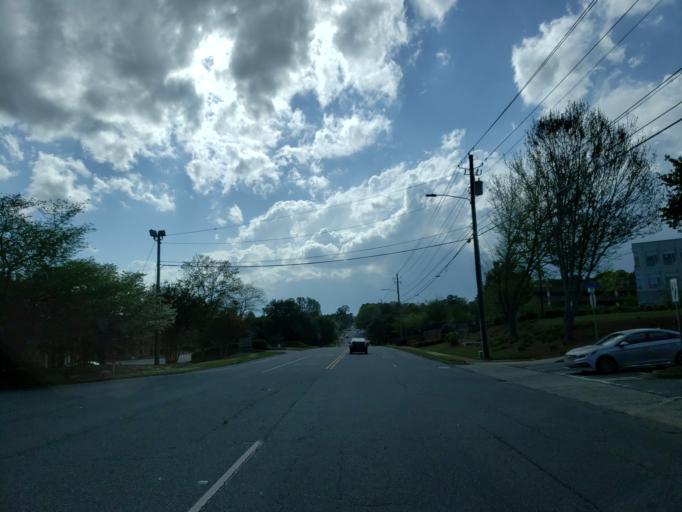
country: US
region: Georgia
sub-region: Fulton County
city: Alpharetta
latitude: 34.0610
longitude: -84.3191
